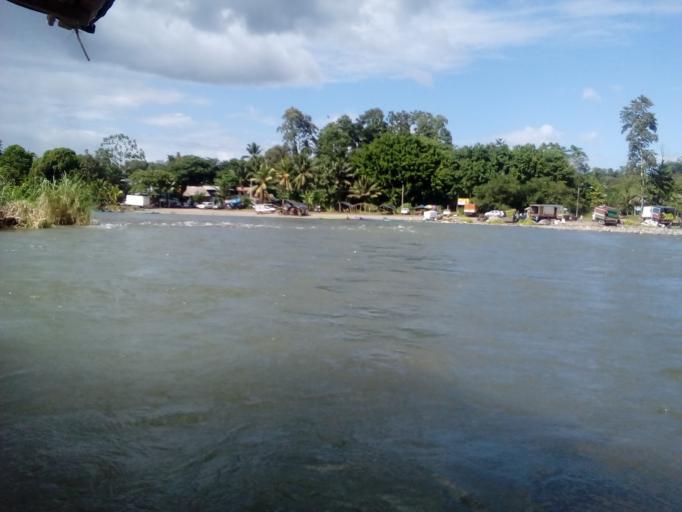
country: PA
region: Bocas del Toro
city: Barranco
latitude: 9.5642
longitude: -82.9360
